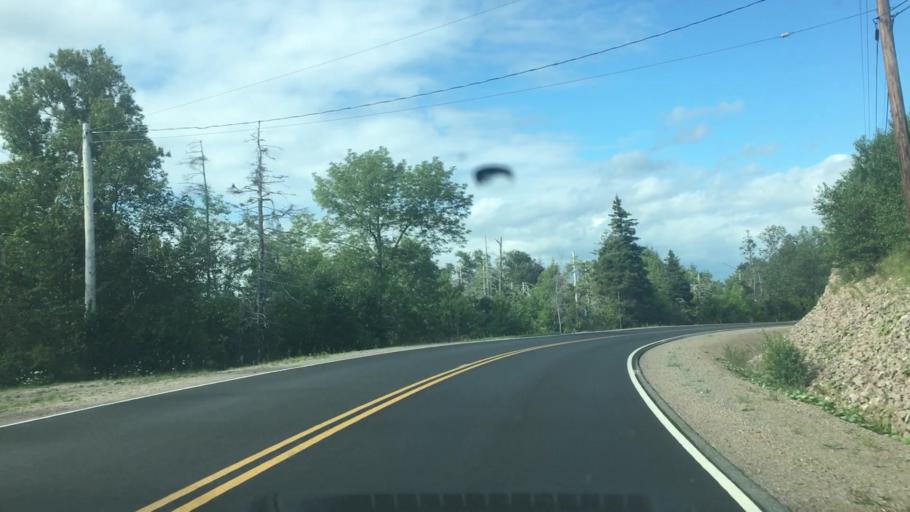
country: CA
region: Nova Scotia
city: Princeville
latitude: 45.7943
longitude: -60.7370
